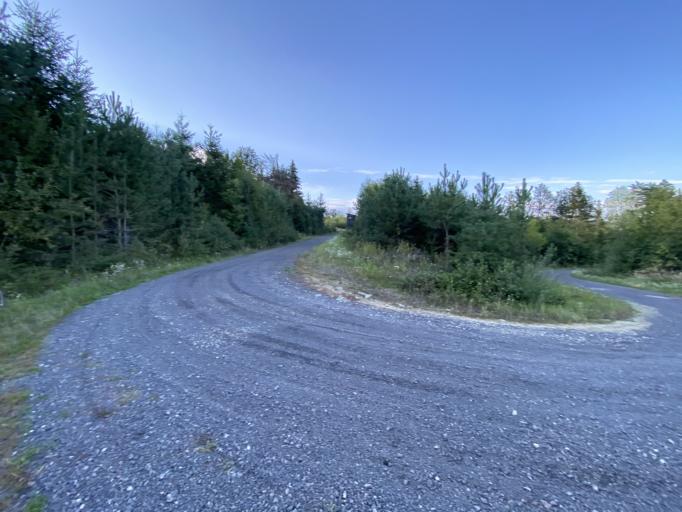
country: AT
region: Burgenland
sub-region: Politischer Bezirk Oberpullendorf
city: Kobersdorf
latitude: 47.5857
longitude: 16.3796
